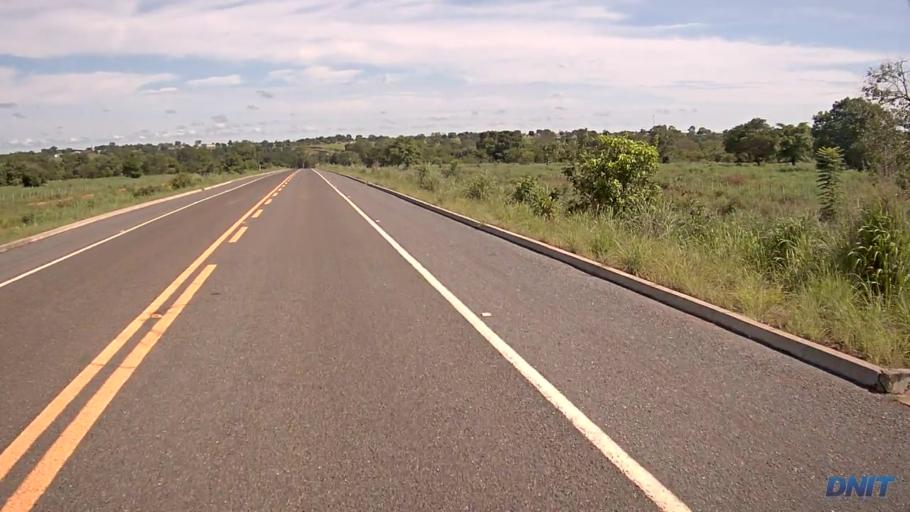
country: BR
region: Goias
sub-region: Sao Miguel Do Araguaia
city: Sao Miguel do Araguaia
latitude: -13.3021
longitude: -50.1745
